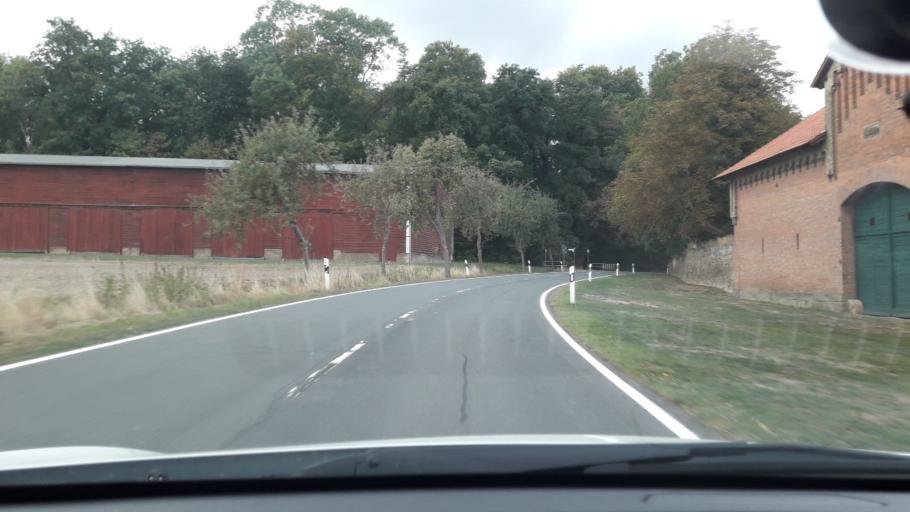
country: DE
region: Lower Saxony
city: Gielde
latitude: 52.0518
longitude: 10.4917
